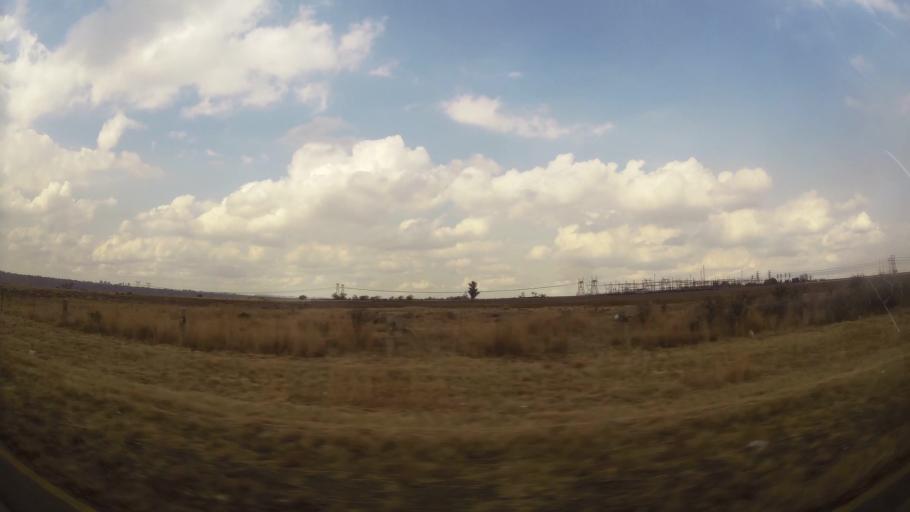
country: ZA
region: Orange Free State
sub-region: Fezile Dabi District Municipality
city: Sasolburg
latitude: -26.8188
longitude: 27.9057
